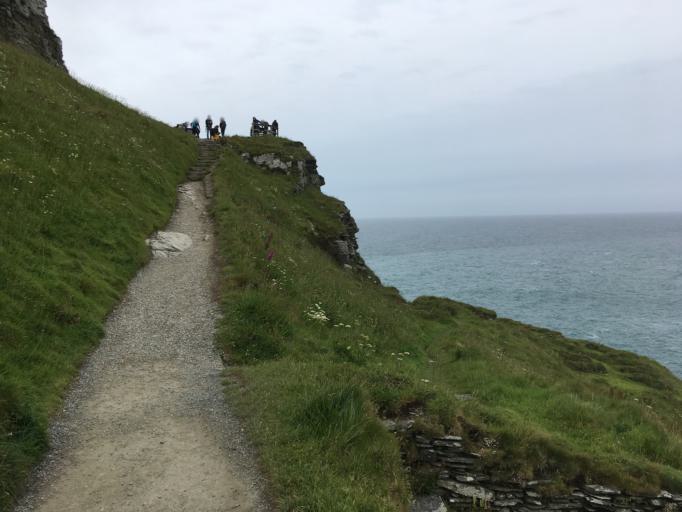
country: GB
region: England
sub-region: Cornwall
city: Tintagel
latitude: 50.6687
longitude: -4.7602
